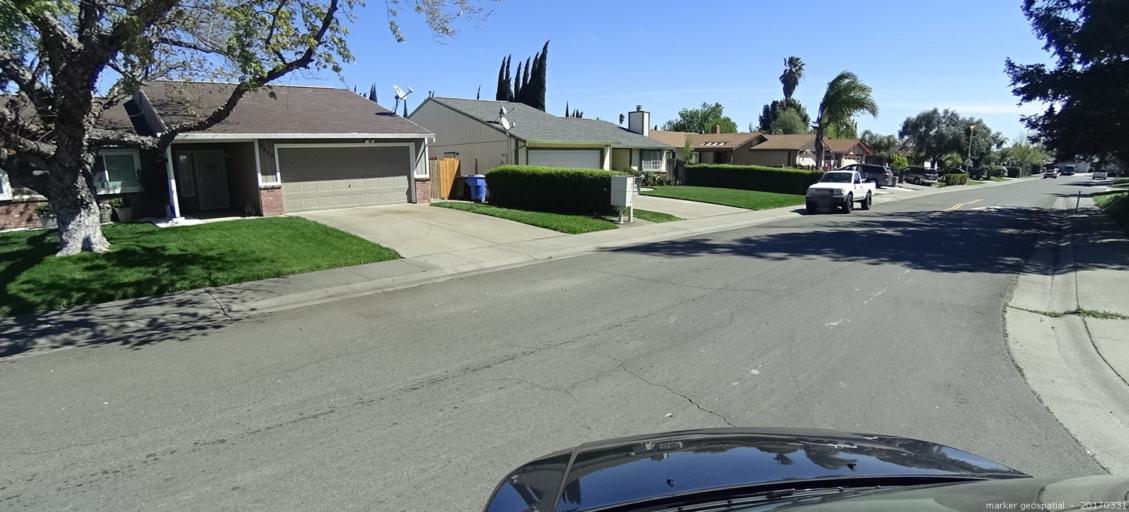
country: US
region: California
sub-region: Sacramento County
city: Parkway
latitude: 38.4637
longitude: -121.4378
